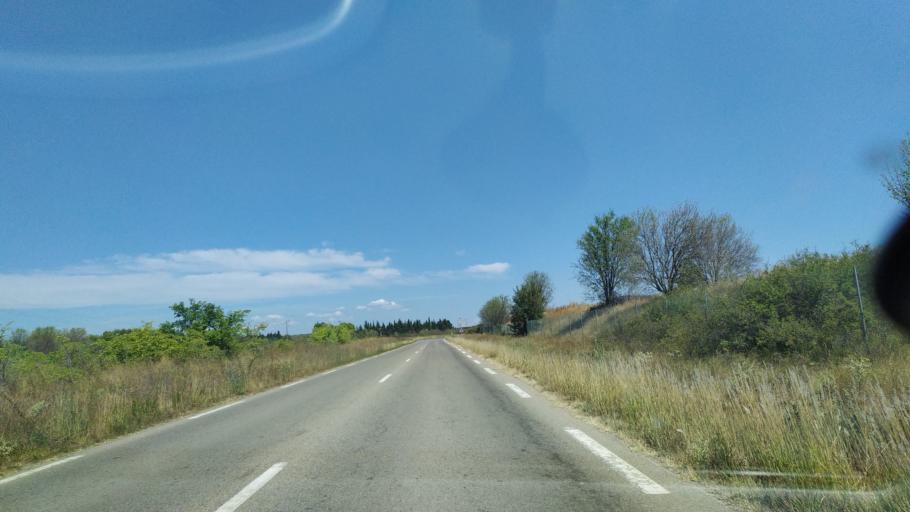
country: FR
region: Languedoc-Roussillon
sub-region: Departement du Gard
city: Codognan
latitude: 43.7185
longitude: 4.2223
